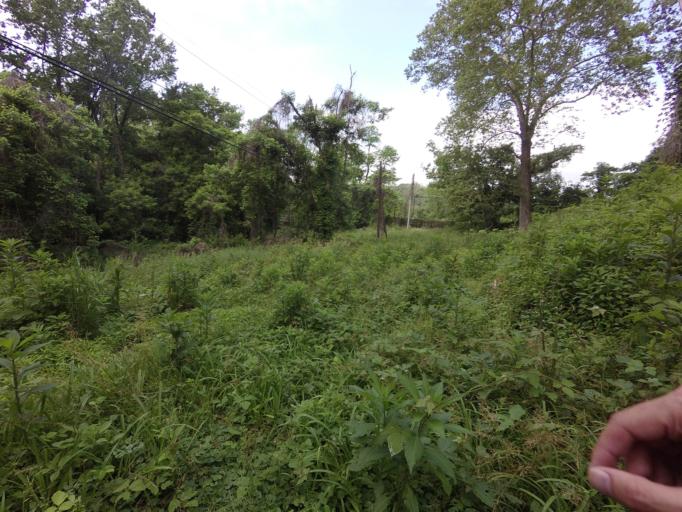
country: US
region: Maryland
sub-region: Baltimore County
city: Lutherville
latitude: 39.3905
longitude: -76.6389
